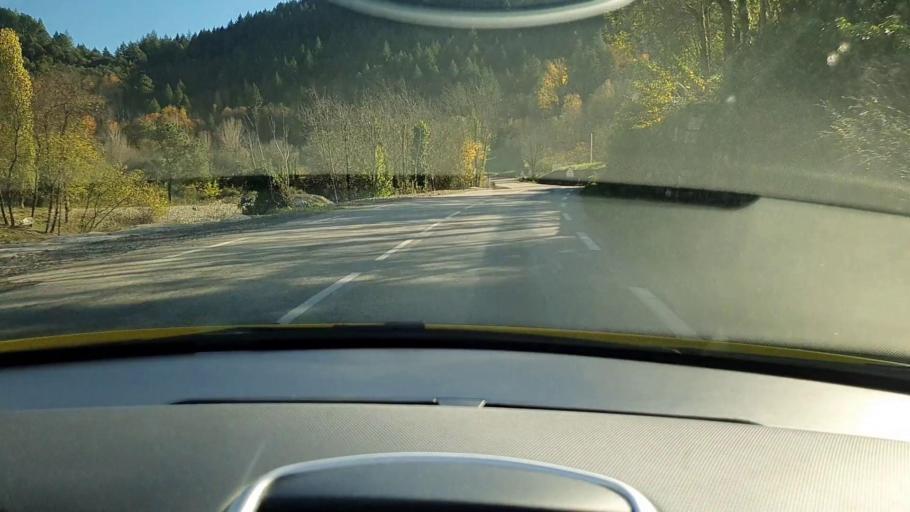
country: FR
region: Languedoc-Roussillon
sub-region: Departement du Gard
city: Lasalle
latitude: 44.1139
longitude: 3.7675
